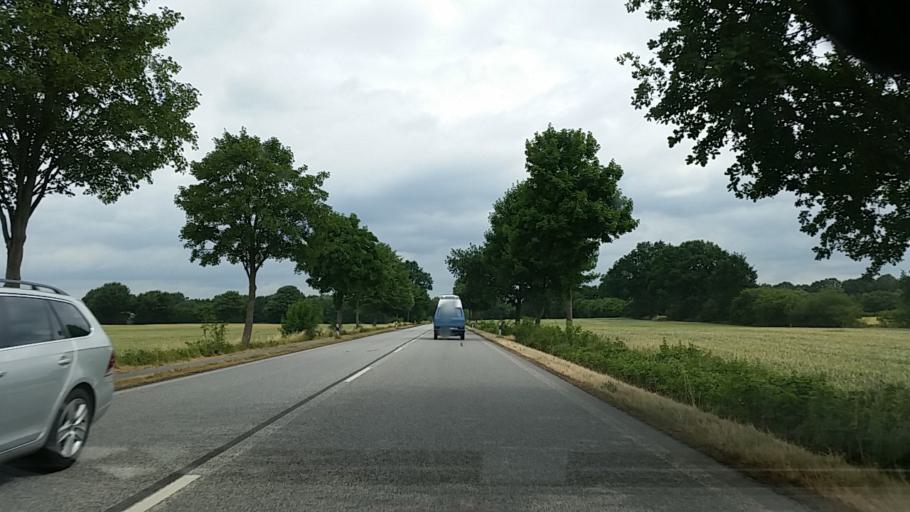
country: DE
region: Schleswig-Holstein
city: Elmenhorst
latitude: 53.7727
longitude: 10.2699
